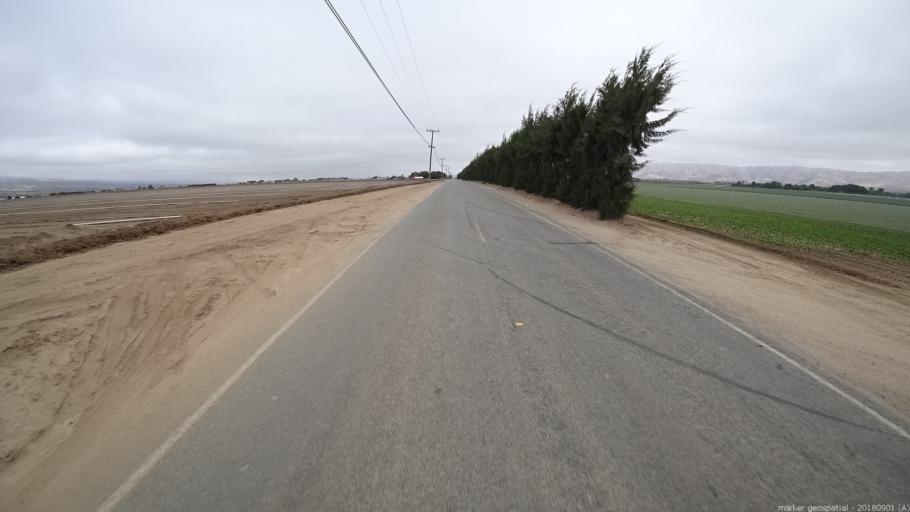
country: US
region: California
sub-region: Monterey County
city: Soledad
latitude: 36.3878
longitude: -121.3318
